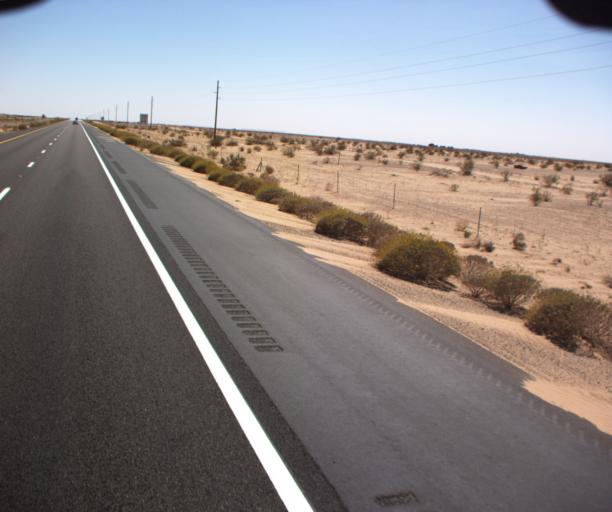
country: US
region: Arizona
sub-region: Yuma County
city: Somerton
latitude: 32.5287
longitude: -114.5622
